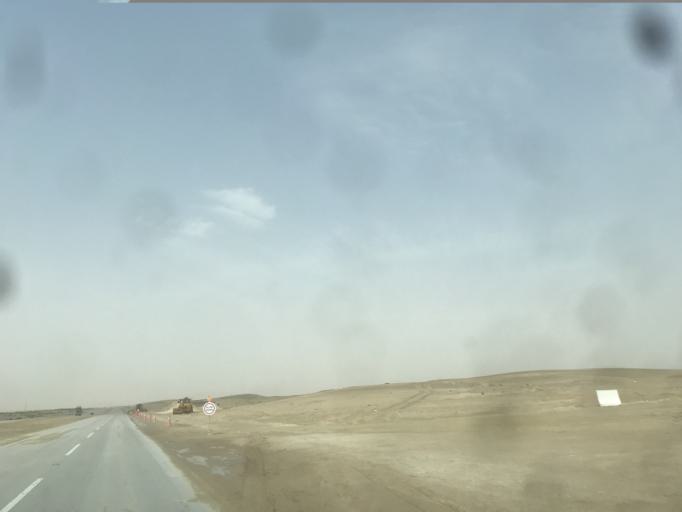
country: SA
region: Eastern Province
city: Abqaiq
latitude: 25.9089
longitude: 49.8868
